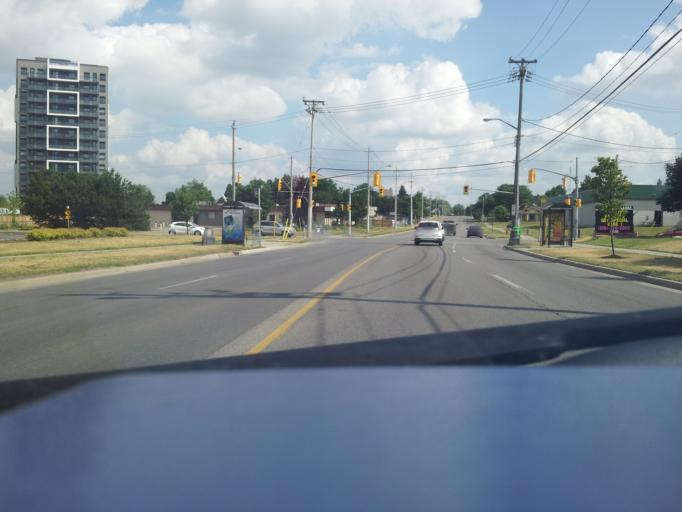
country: CA
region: Ontario
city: Waterloo
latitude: 43.4479
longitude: -80.5144
